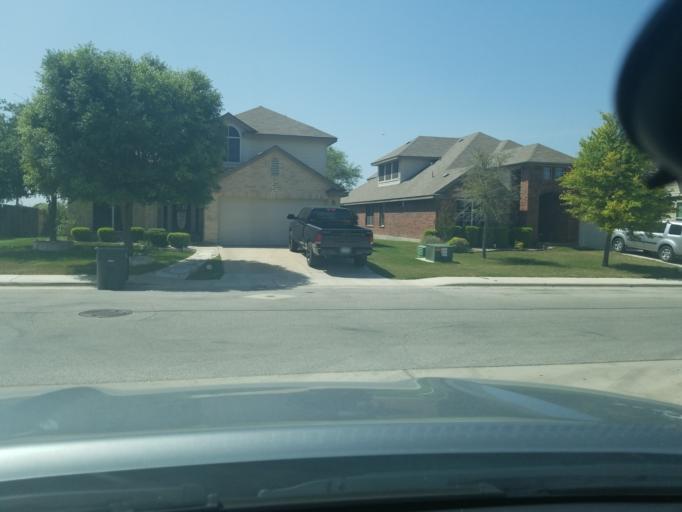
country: US
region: Texas
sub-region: Guadalupe County
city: Lake Dunlap
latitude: 29.6736
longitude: -98.0393
